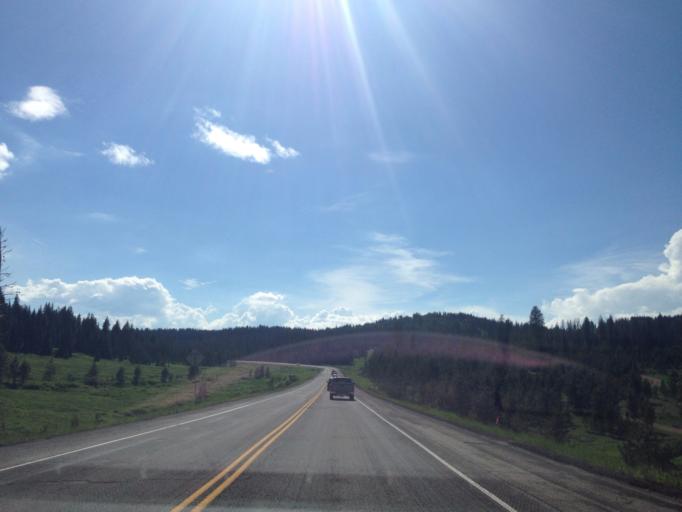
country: US
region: Colorado
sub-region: Routt County
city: Steamboat Springs
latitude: 40.3759
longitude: -106.7266
